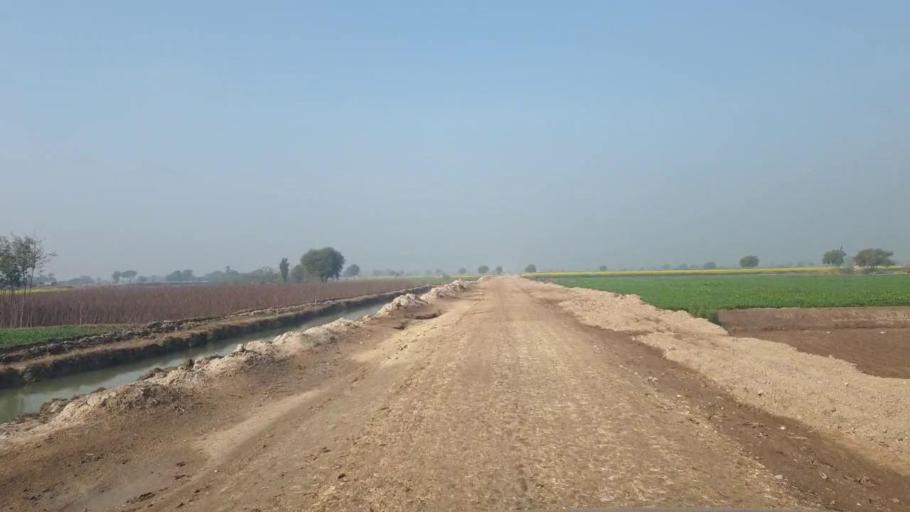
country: PK
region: Sindh
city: Shahdadpur
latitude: 25.9509
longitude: 68.5727
